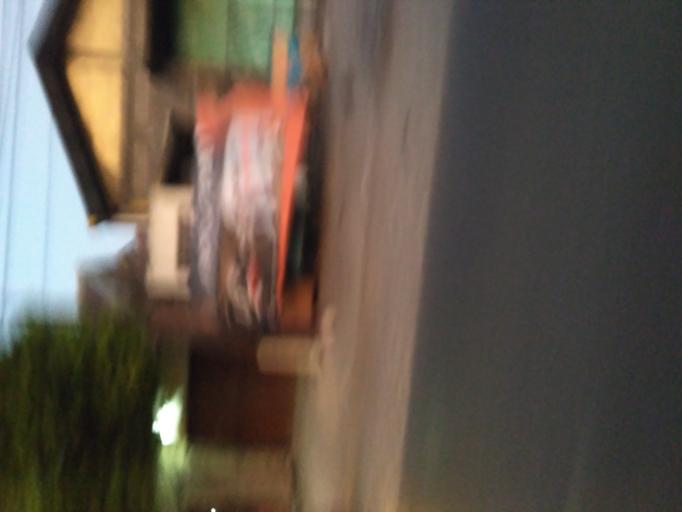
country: ID
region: Daerah Istimewa Yogyakarta
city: Kasihan
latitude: -7.8270
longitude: 110.3735
